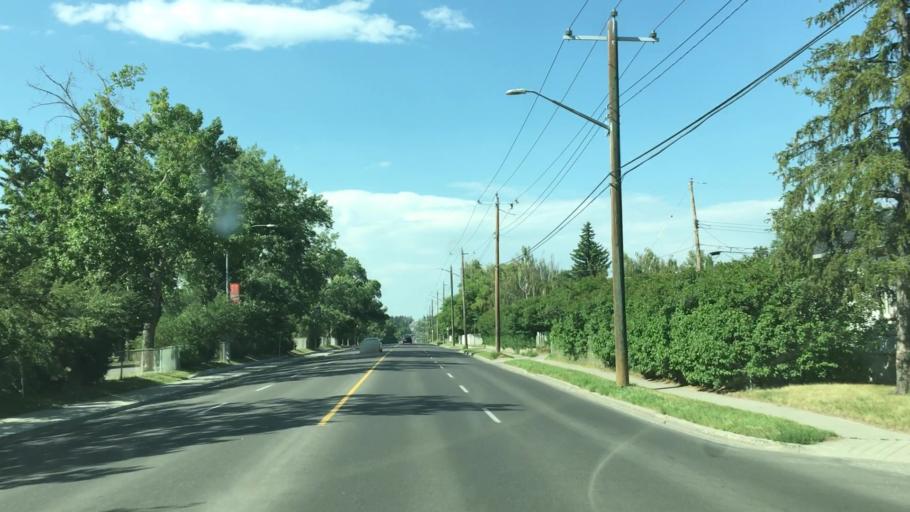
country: CA
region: Alberta
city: Calgary
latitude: 51.0824
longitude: -114.0715
